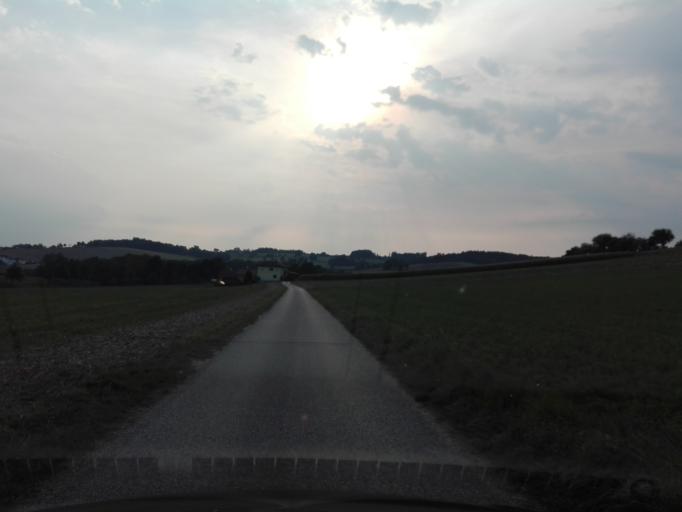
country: AT
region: Upper Austria
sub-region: Politischer Bezirk Grieskirchen
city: Grieskirchen
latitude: 48.2526
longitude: 13.8215
